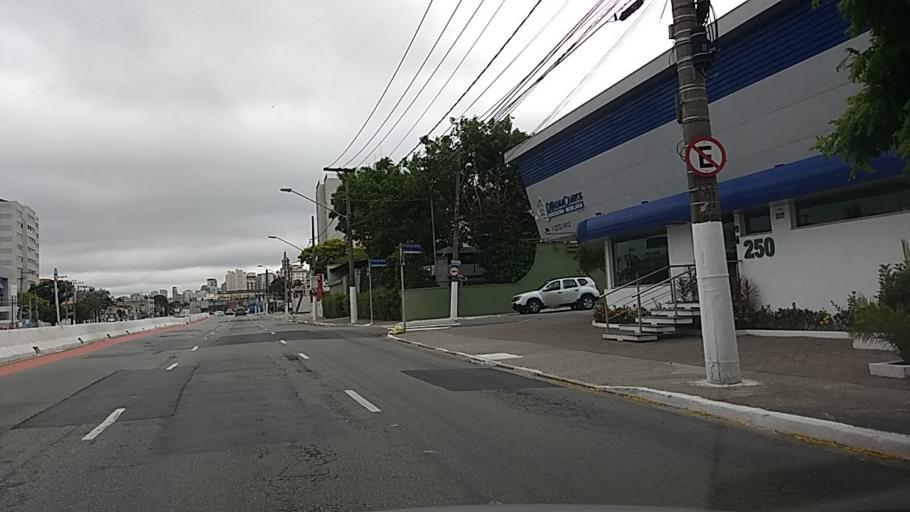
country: BR
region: Sao Paulo
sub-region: Sao Paulo
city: Sao Paulo
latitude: -23.5799
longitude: -46.6130
